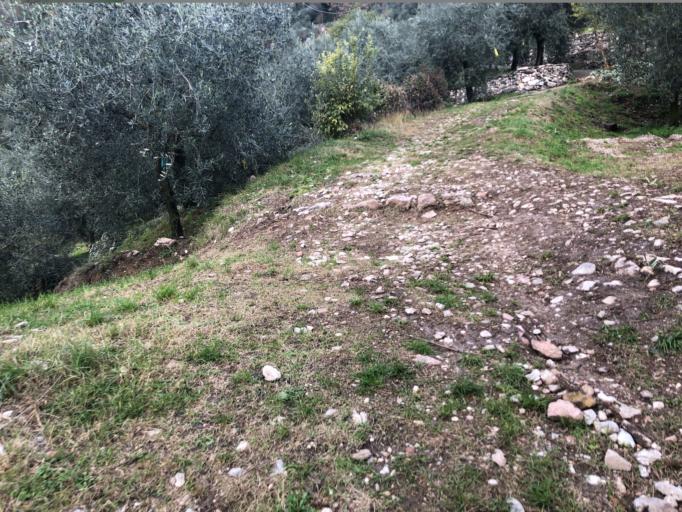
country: IT
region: Trentino-Alto Adige
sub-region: Provincia di Trento
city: Tenno
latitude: 45.9133
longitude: 10.8387
